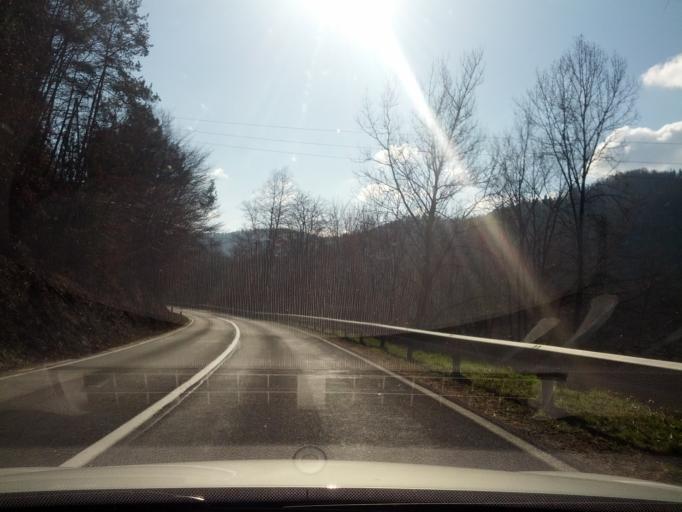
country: SI
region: Moravce
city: Moravce
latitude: 46.0926
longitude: 14.6953
